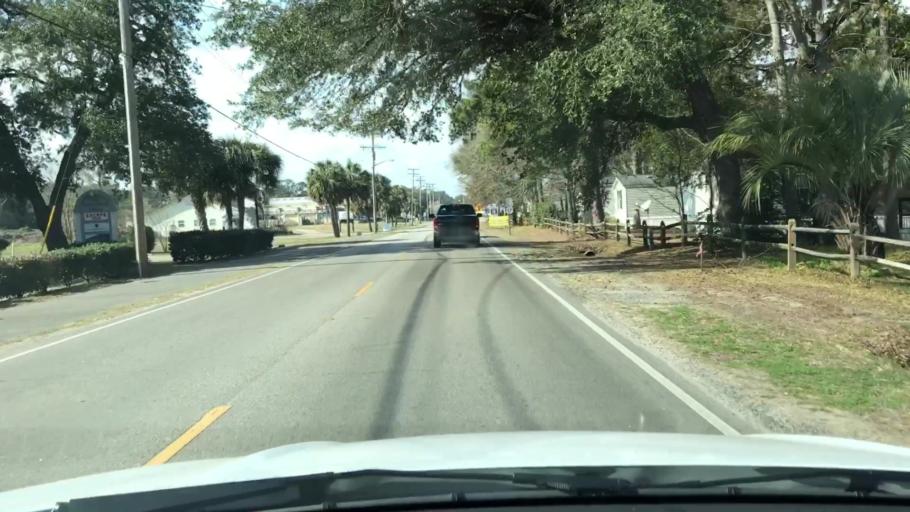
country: US
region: South Carolina
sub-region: Horry County
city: Garden City
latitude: 33.5838
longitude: -79.0094
